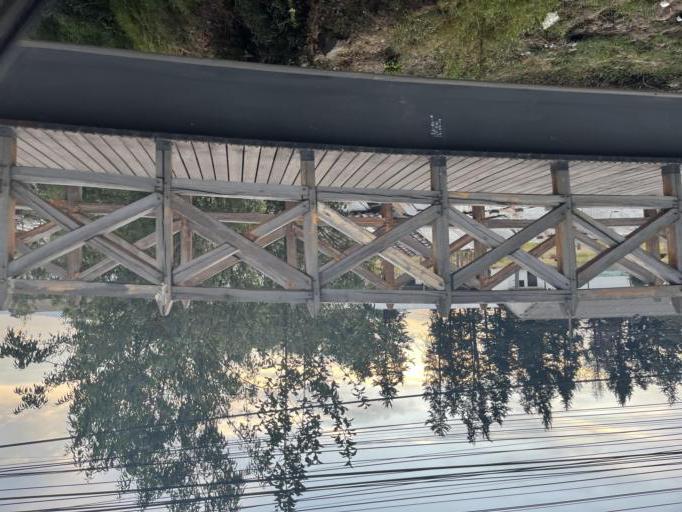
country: EC
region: Pichincha
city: Cayambe
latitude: 0.0619
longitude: -78.1363
